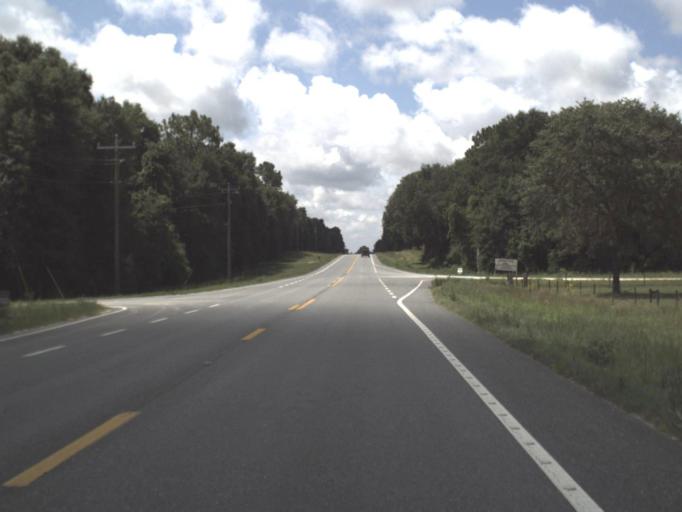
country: US
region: Florida
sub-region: Gilchrist County
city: Trenton
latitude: 29.8755
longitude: -82.8598
